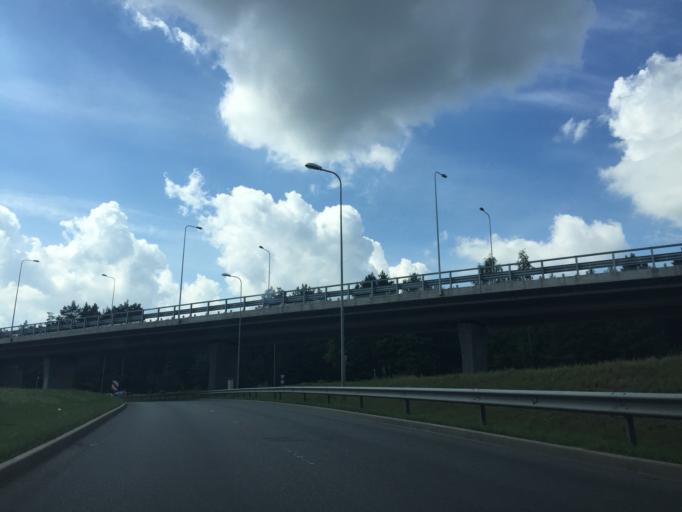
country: LV
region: Kekava
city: Balozi
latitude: 56.9019
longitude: 24.1337
